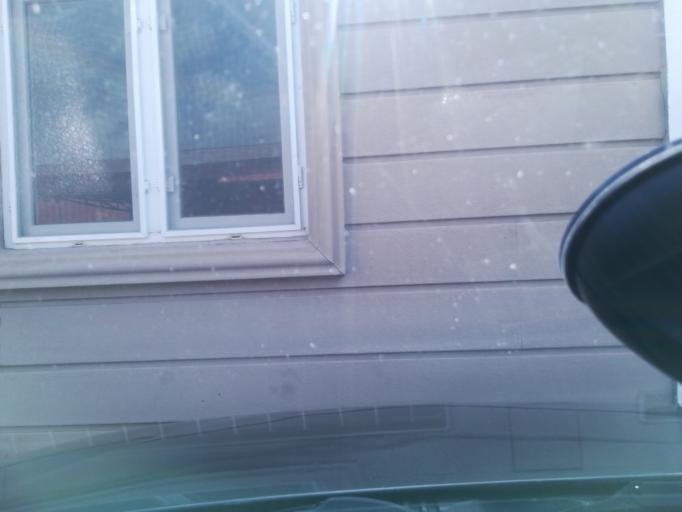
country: TR
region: Adana
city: Yuregir
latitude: 36.9846
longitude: 35.4346
